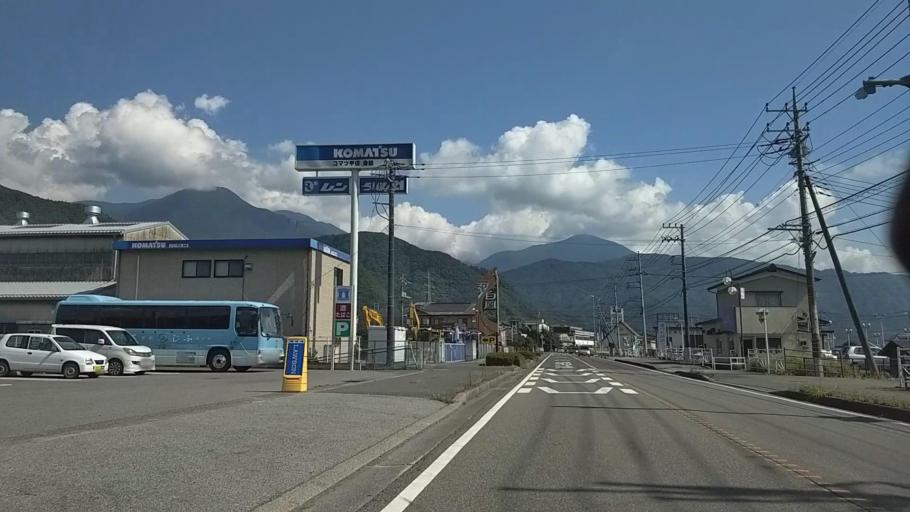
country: JP
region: Yamanashi
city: Ryuo
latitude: 35.4344
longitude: 138.4405
